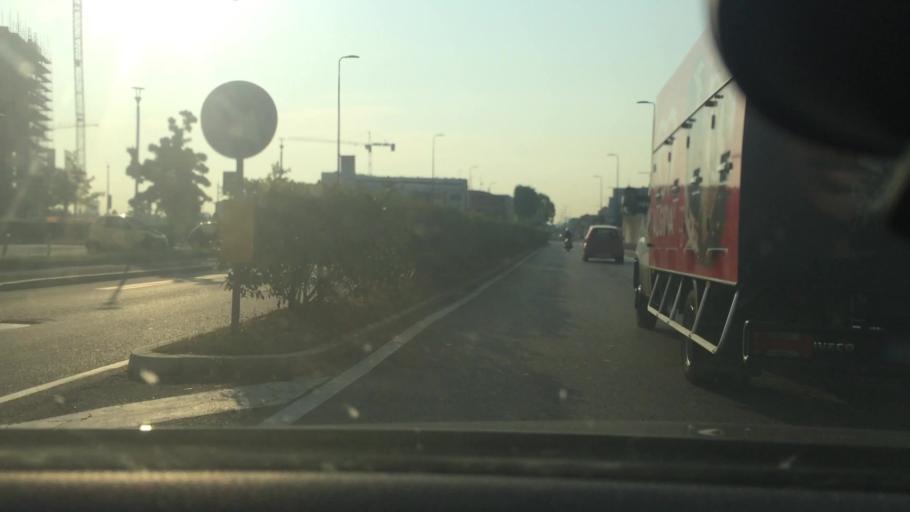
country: IT
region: Lombardy
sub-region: Citta metropolitana di Milano
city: Pero
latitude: 45.5066
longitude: 9.0988
